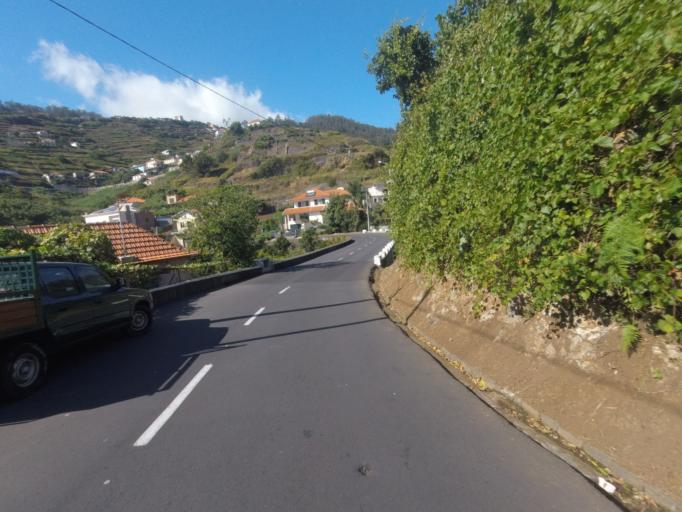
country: PT
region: Madeira
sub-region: Ribeira Brava
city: Campanario
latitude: 32.6745
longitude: -17.0239
